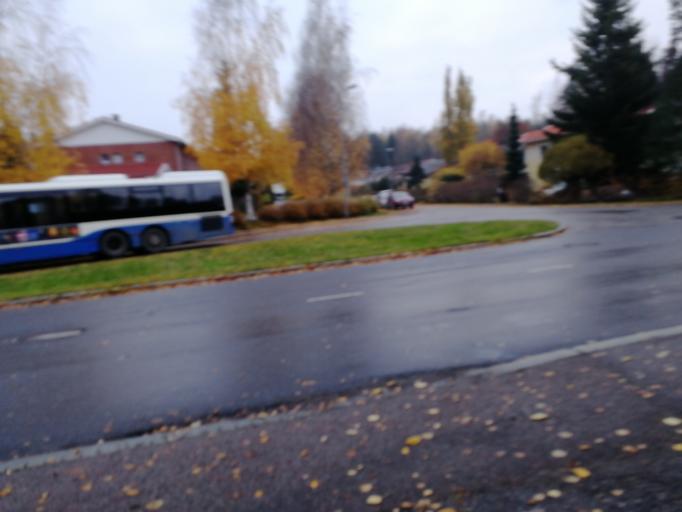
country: FI
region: Pirkanmaa
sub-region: Tampere
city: Tampere
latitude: 61.4447
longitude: 23.8727
